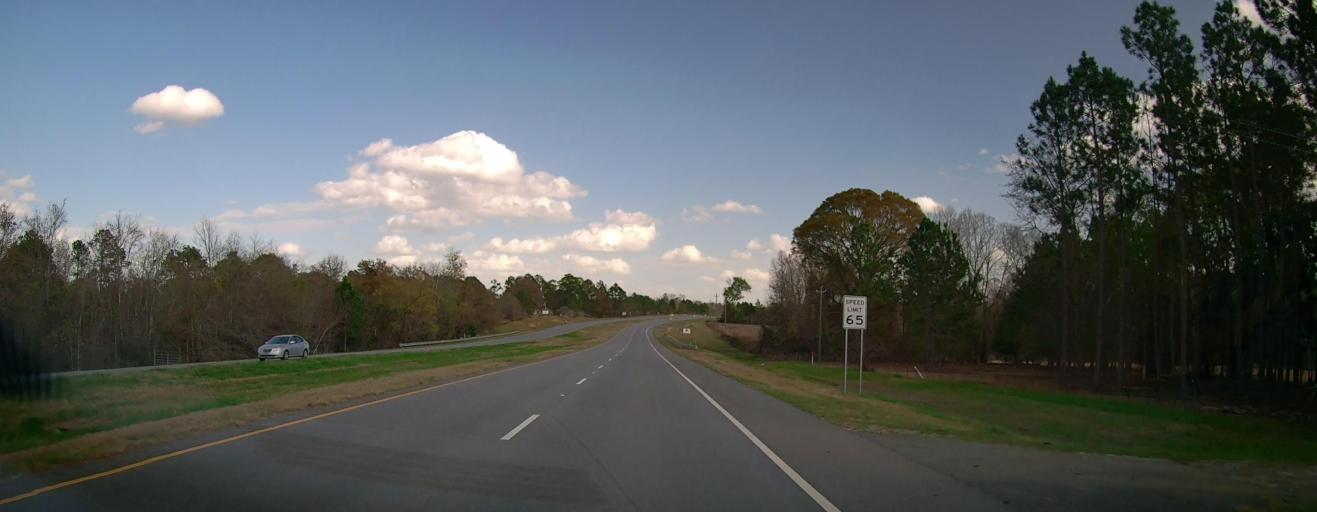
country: US
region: Georgia
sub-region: Telfair County
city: Helena
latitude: 32.1035
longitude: -82.9636
